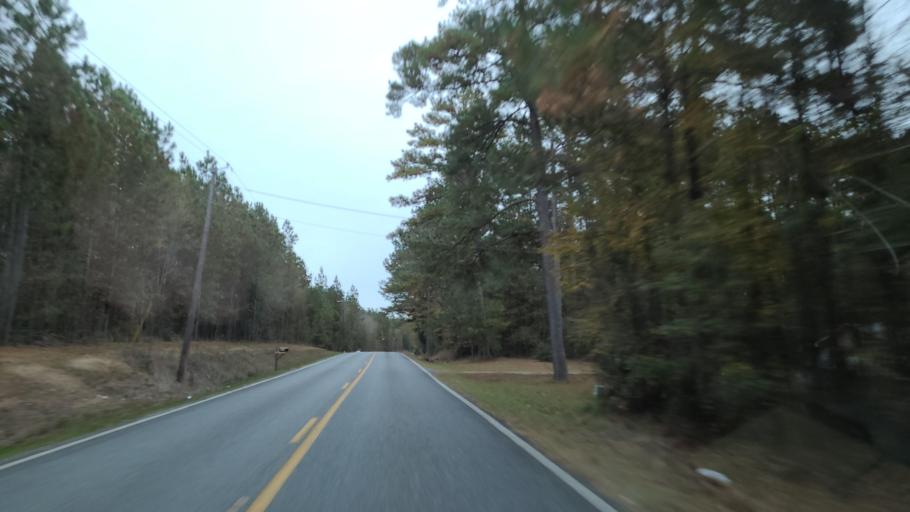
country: US
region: Mississippi
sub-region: Clarke County
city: Quitman
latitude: 32.0296
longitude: -88.8261
